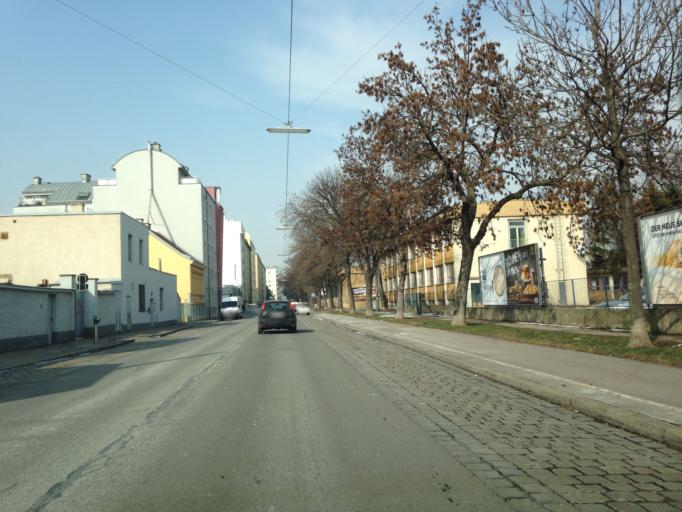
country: AT
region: Vienna
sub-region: Wien Stadt
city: Vienna
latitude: 48.2321
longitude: 16.3779
